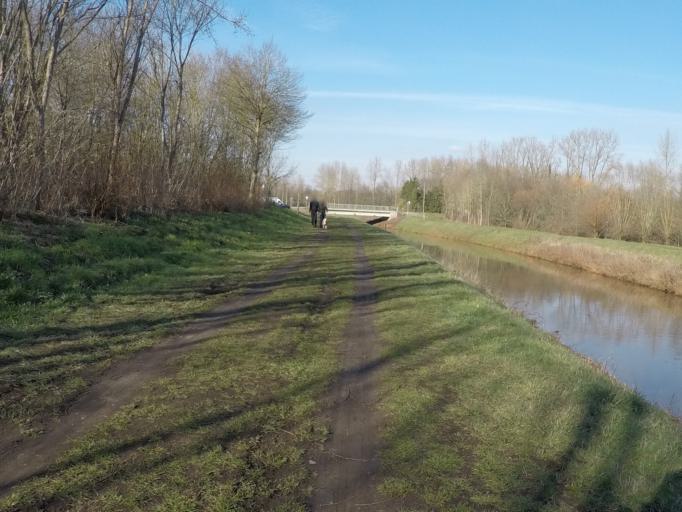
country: BE
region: Flanders
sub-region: Provincie Antwerpen
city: Heist-op-den-Berg
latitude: 51.0769
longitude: 4.7572
